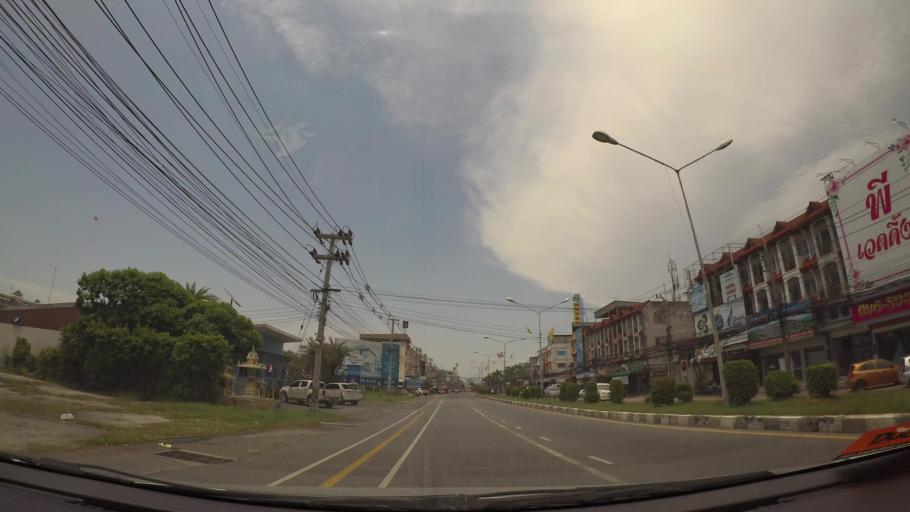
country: TH
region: Chon Buri
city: Chon Buri
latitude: 13.3399
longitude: 100.9575
